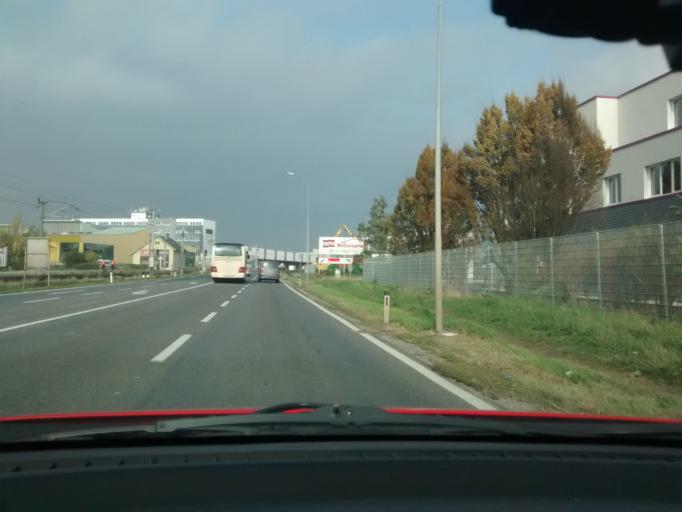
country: AT
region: Lower Austria
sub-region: Politischer Bezirk Modling
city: Neu-Guntramsdorf
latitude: 48.0719
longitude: 16.3122
